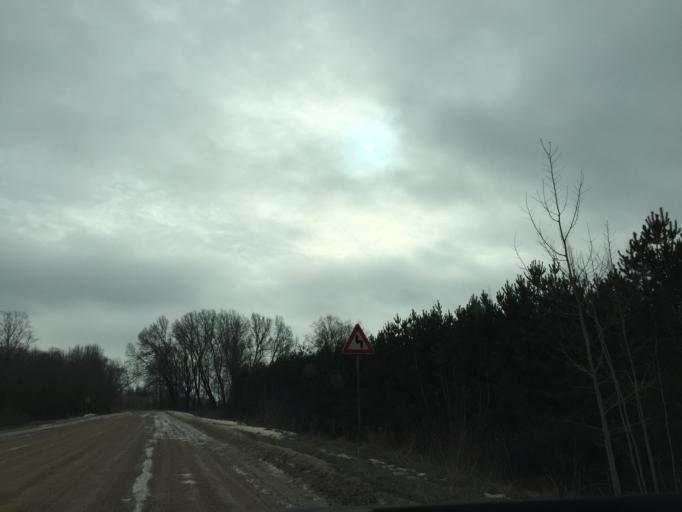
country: LV
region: Rundales
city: Pilsrundale
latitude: 56.5387
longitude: 23.9956
